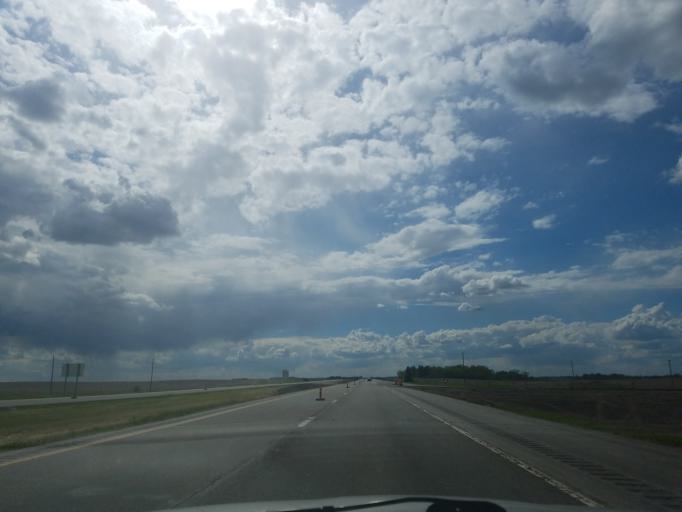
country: US
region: North Dakota
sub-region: Barnes County
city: Valley City
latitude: 46.9200
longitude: -97.7893
